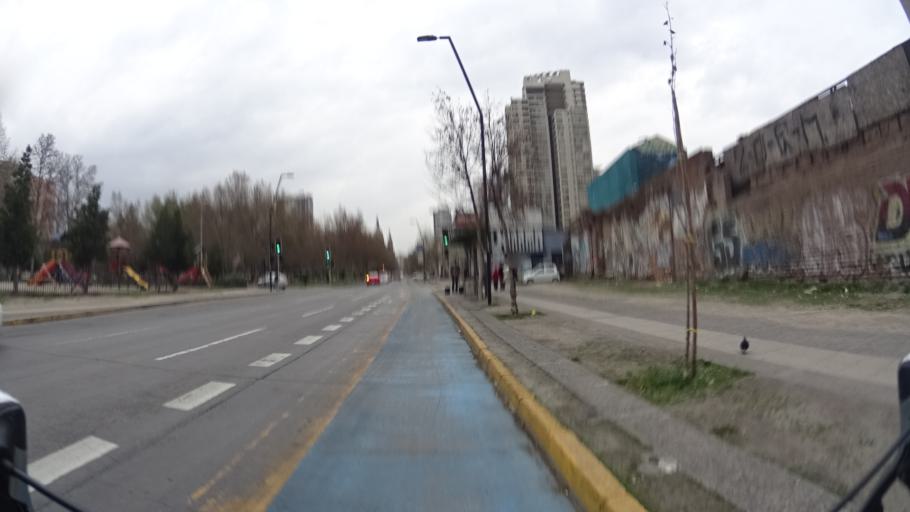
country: CL
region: Santiago Metropolitan
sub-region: Provincia de Santiago
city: Santiago
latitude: -33.4529
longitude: -70.6546
